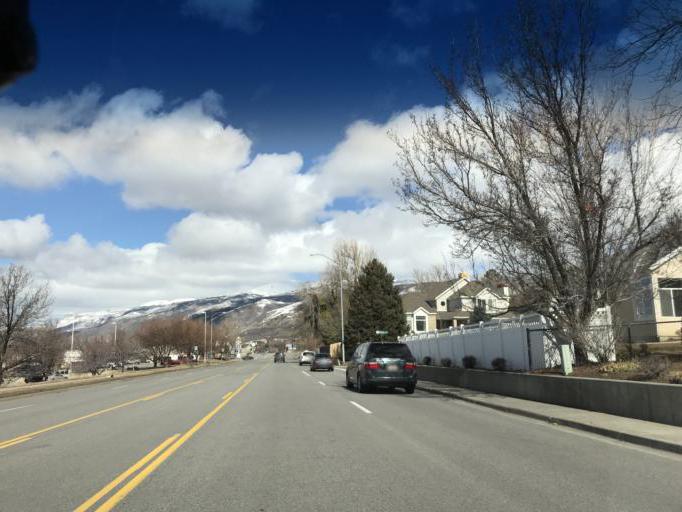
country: US
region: Utah
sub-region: Davis County
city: Woods Cross
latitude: 40.8644
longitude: -111.8801
